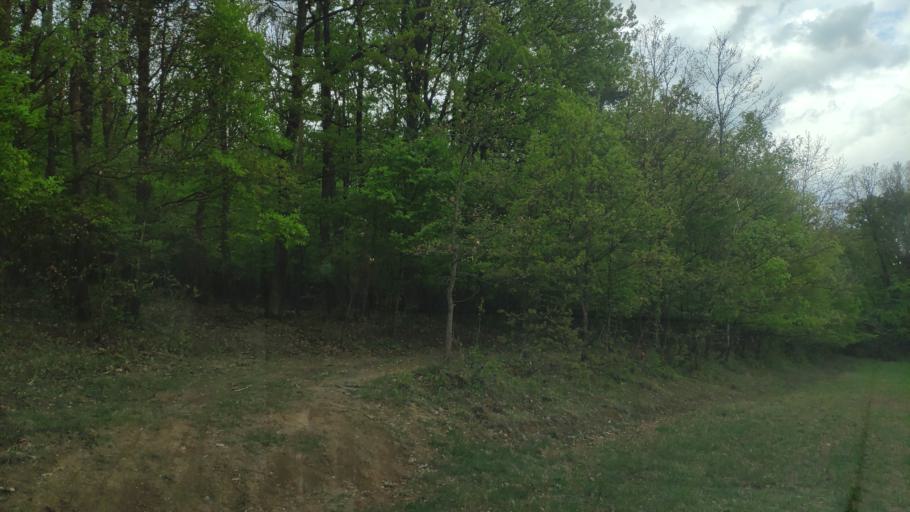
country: SK
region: Kosicky
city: Moldava nad Bodvou
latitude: 48.5436
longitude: 20.9329
